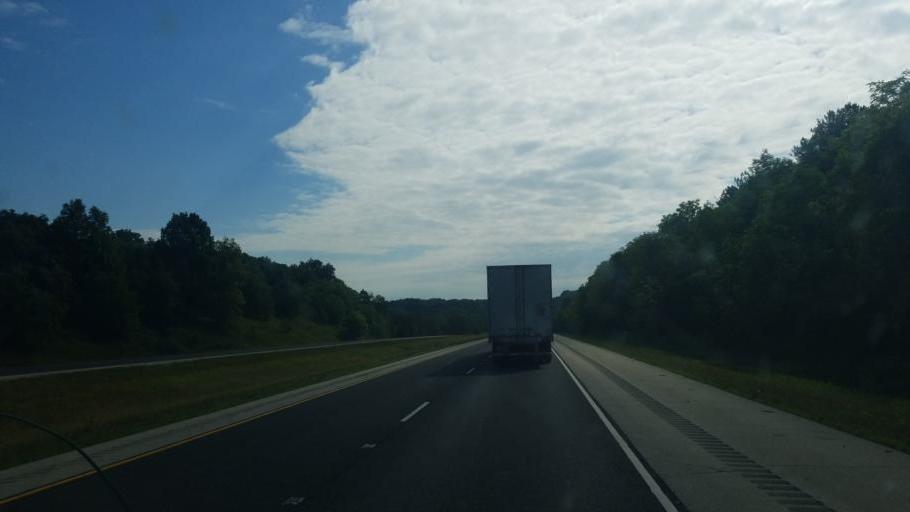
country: US
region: Illinois
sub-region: Clark County
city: Marshall
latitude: 39.3926
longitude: -87.7956
